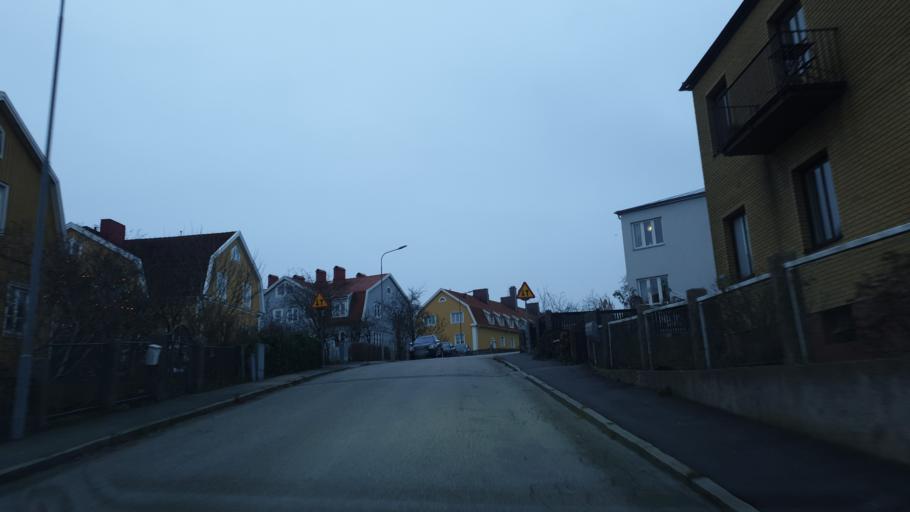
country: SE
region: Blekinge
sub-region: Karlskrona Kommun
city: Karlskrona
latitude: 56.1686
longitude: 15.5680
